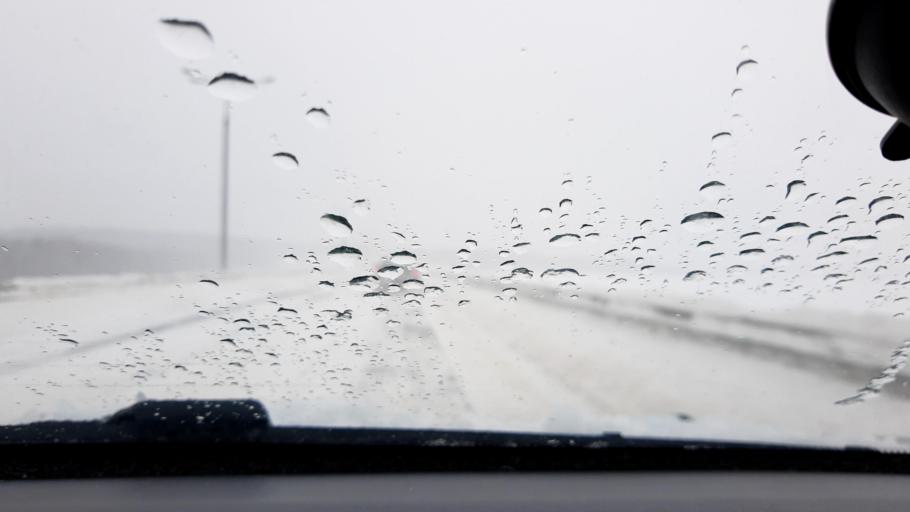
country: RU
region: Nizjnij Novgorod
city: Pervomayskiy
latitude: 56.6386
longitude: 43.2670
